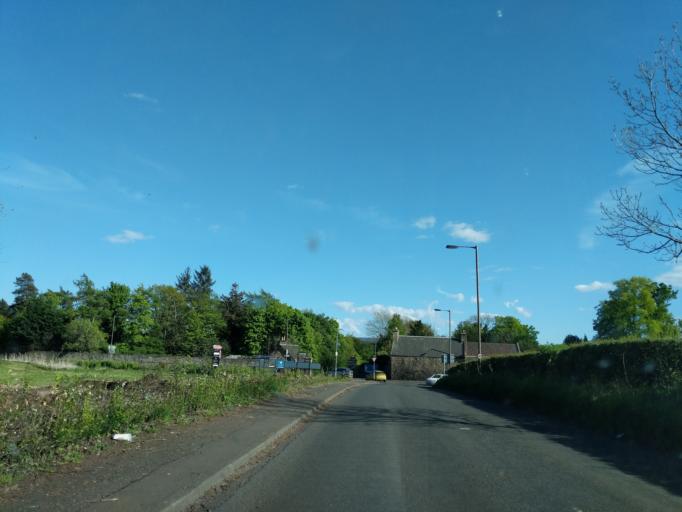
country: GB
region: Scotland
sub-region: Edinburgh
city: Ratho
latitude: 55.9087
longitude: -3.3693
